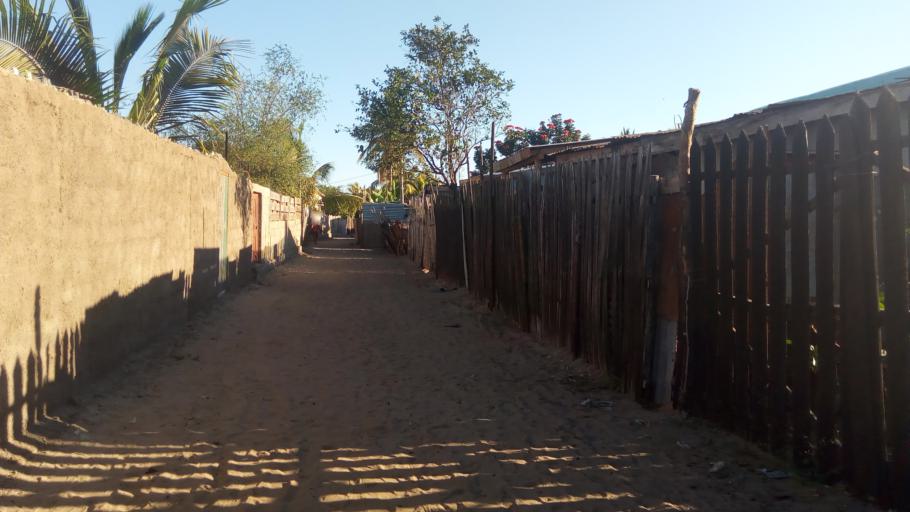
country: MG
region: Menabe
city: Morondava
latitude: -20.2968
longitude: 44.2785
